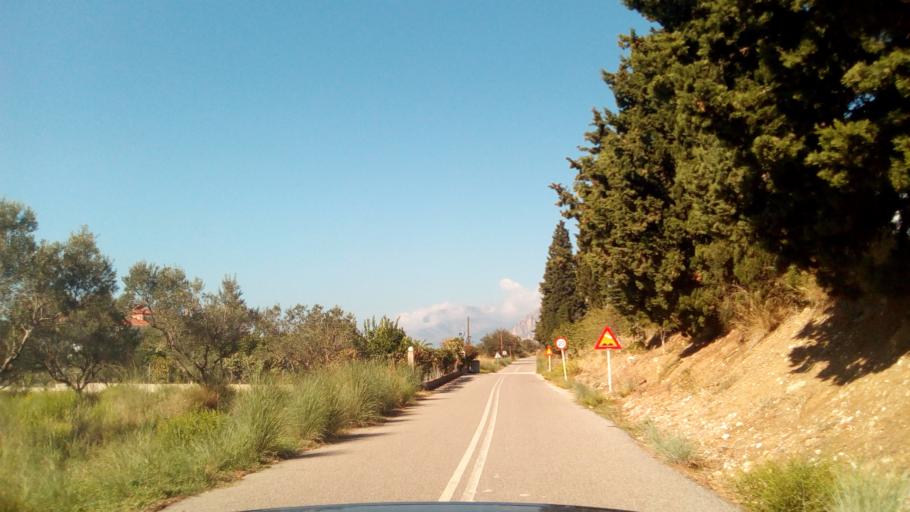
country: GR
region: West Greece
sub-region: Nomos Aitolias kai Akarnanias
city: Antirrio
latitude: 38.3381
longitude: 21.7408
